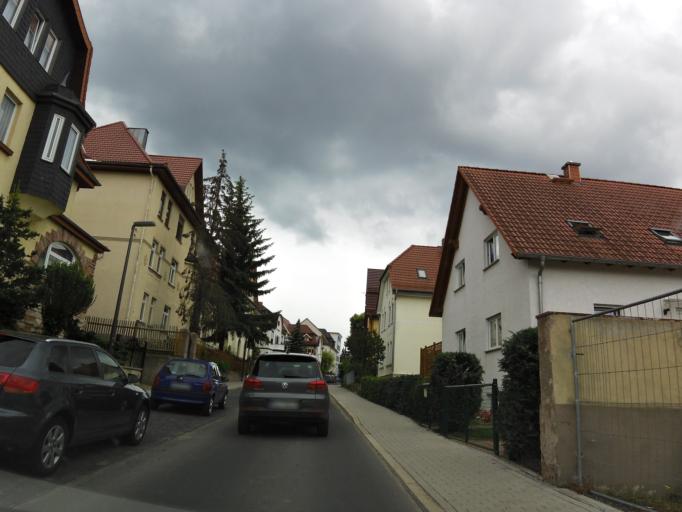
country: DE
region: Thuringia
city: Bad Salzungen
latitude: 50.8140
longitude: 10.2283
